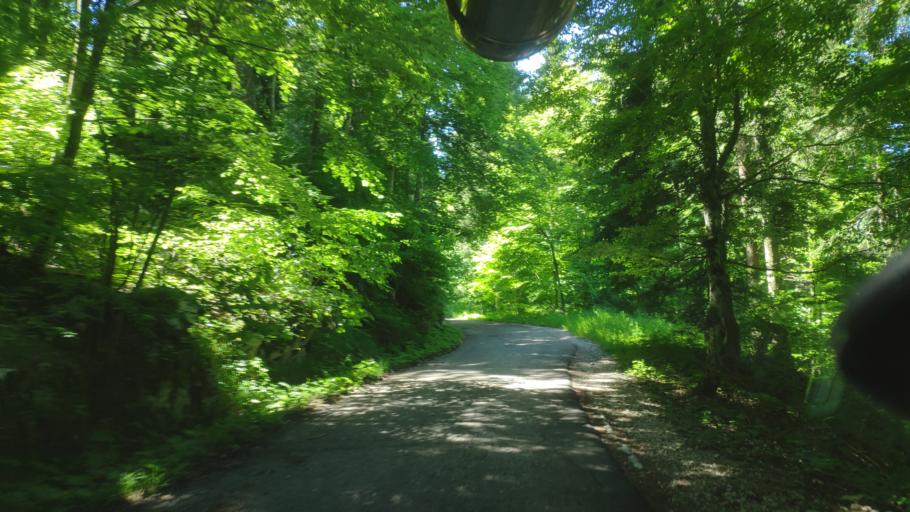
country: IT
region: Veneto
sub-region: Provincia di Vicenza
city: Cogollo del Cengio
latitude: 45.8244
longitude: 11.4429
